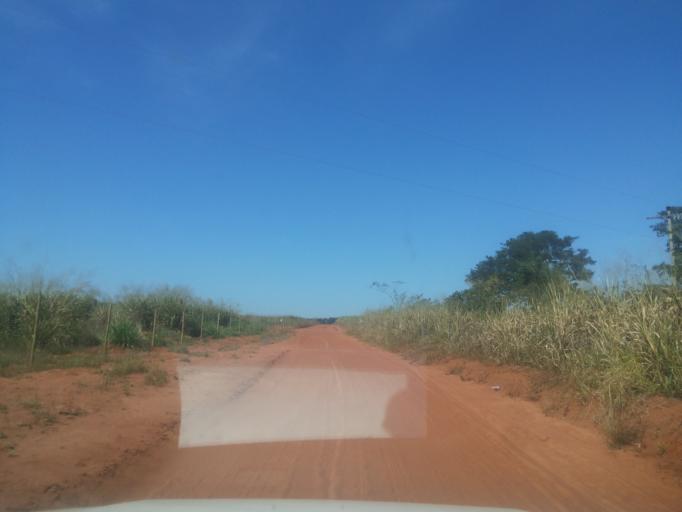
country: BR
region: Minas Gerais
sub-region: Santa Vitoria
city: Santa Vitoria
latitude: -18.9940
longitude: -50.3750
